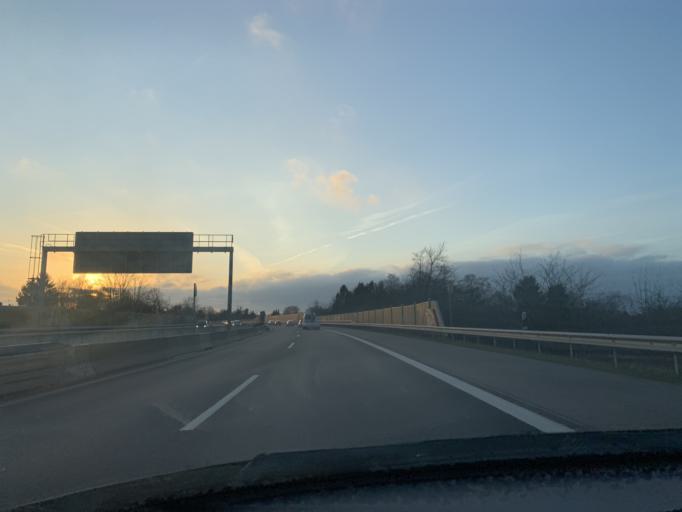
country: DE
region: Lower Saxony
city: Oldenburg
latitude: 53.1630
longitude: 8.2081
